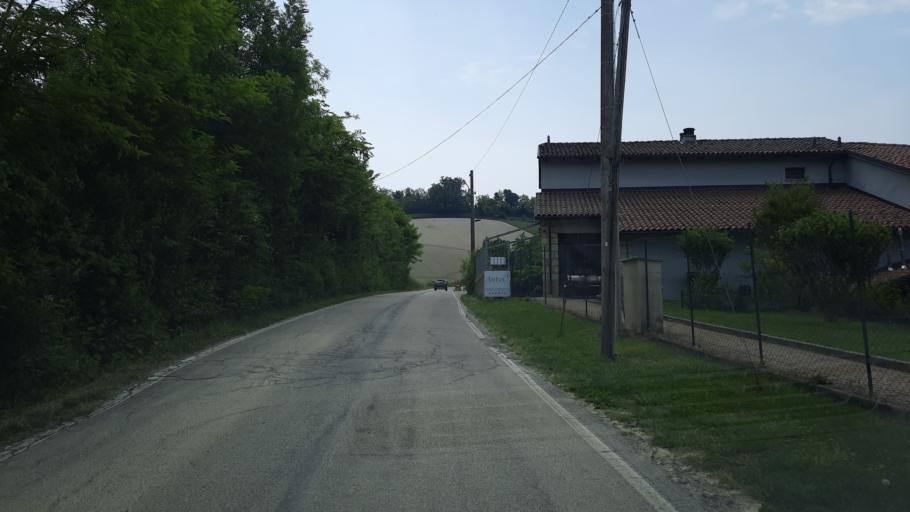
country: IT
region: Piedmont
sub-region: Provincia di Alessandria
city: Ozzano Monferrato
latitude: 45.0991
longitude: 8.3854
